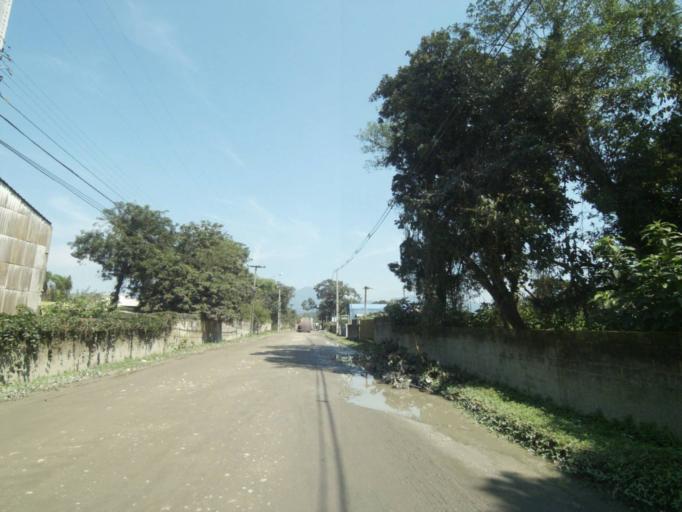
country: BR
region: Parana
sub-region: Paranagua
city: Paranagua
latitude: -25.5491
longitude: -48.5776
